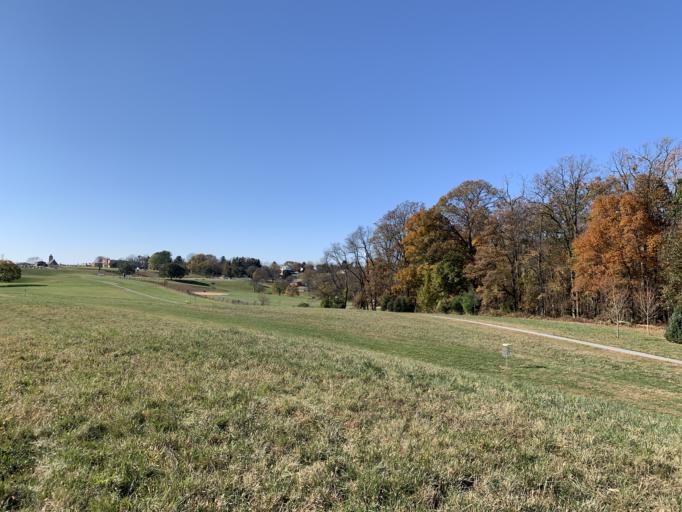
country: US
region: Maryland
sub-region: Carroll County
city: Hampstead
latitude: 39.6084
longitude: -76.8413
